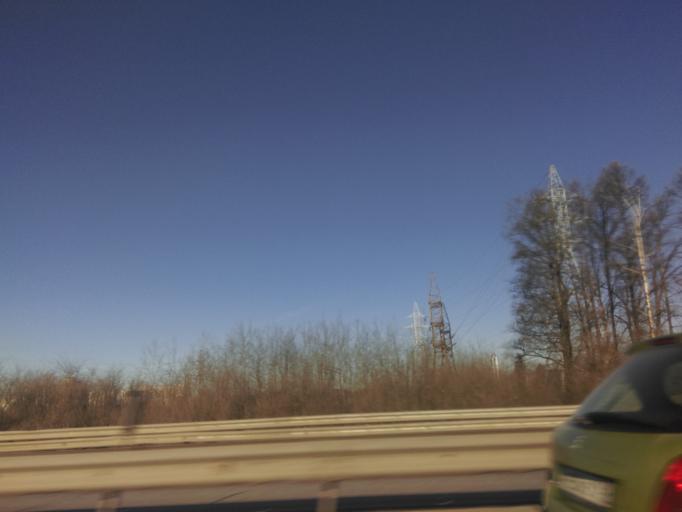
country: RU
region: Moskovskaya
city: Skolkovo
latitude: 55.6873
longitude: 37.3306
